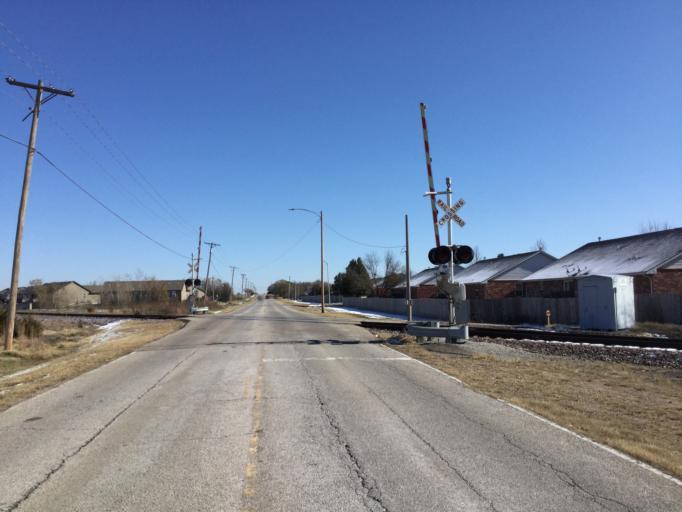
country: US
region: Kansas
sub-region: Sedgwick County
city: Bellaire
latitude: 37.7668
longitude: -97.2390
